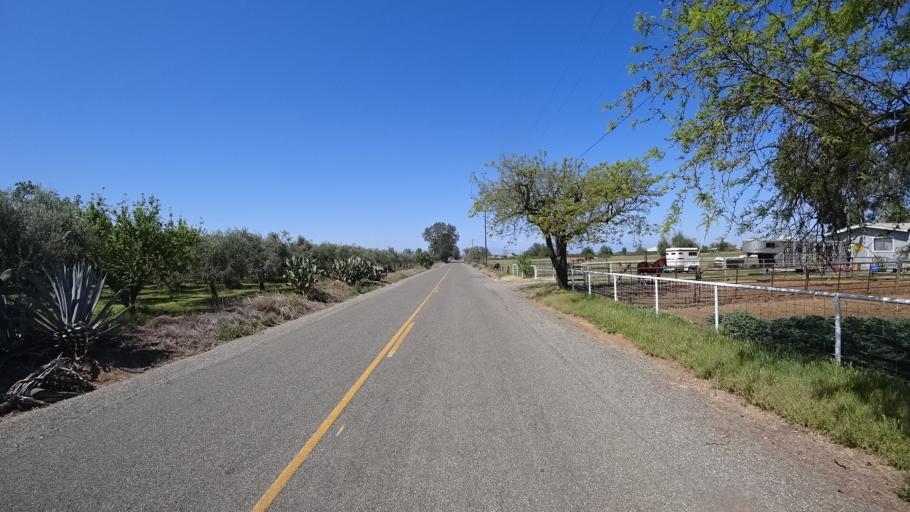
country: US
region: California
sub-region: Glenn County
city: Orland
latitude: 39.7871
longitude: -122.1784
